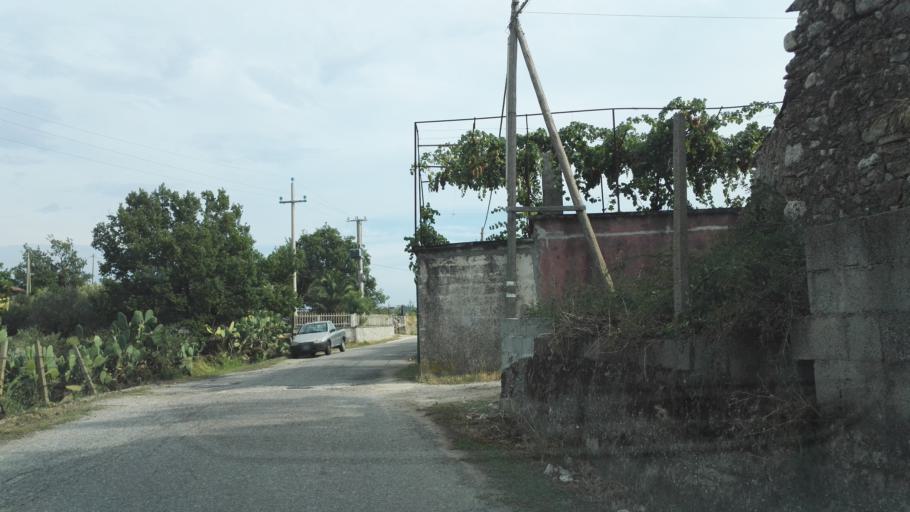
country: IT
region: Calabria
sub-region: Provincia di Reggio Calabria
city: Stignano
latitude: 38.4282
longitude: 16.4623
